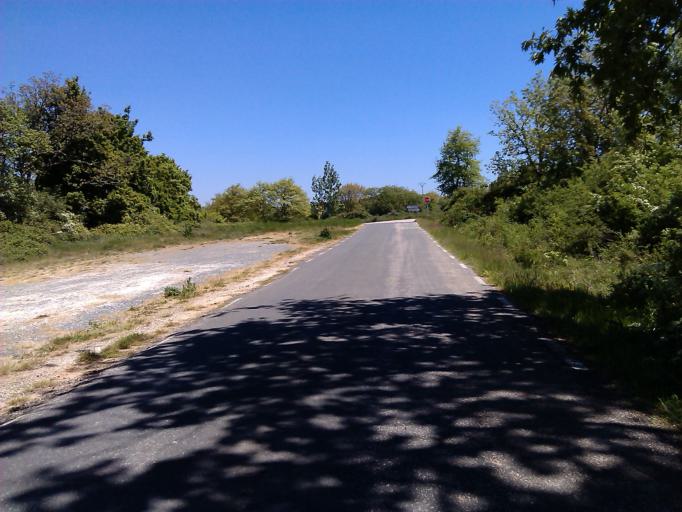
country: ES
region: Castille and Leon
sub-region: Provincia de Burgos
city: Barrios de Colina
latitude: 42.3766
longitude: -3.4421
